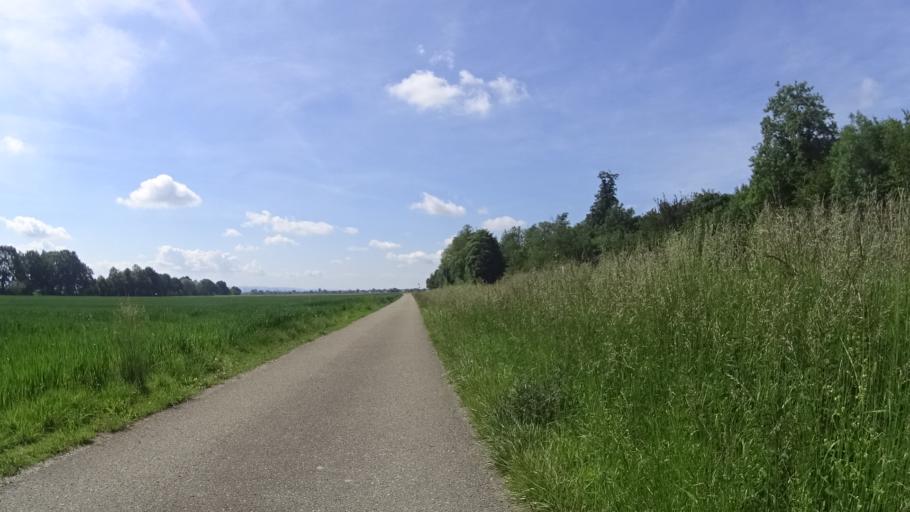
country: DE
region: Baden-Wuerttemberg
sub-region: Freiburg Region
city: Schutterwald
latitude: 48.4855
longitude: 7.8177
